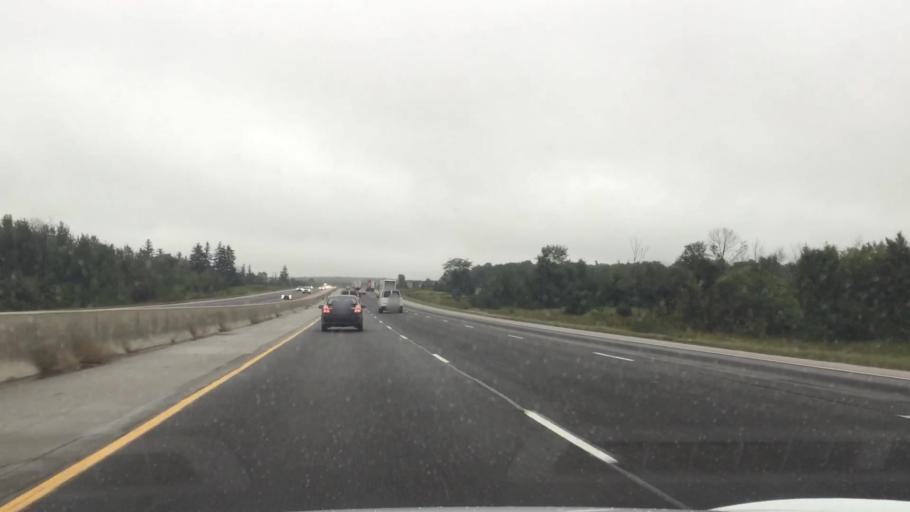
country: CA
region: Ontario
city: Kitchener
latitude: 43.3044
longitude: -80.4814
